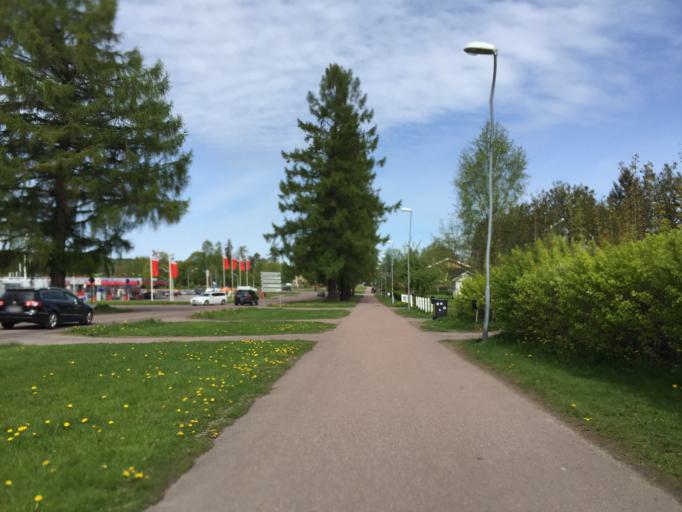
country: SE
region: Dalarna
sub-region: Ludvika Kommun
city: Ludvika
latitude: 60.1298
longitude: 15.1798
